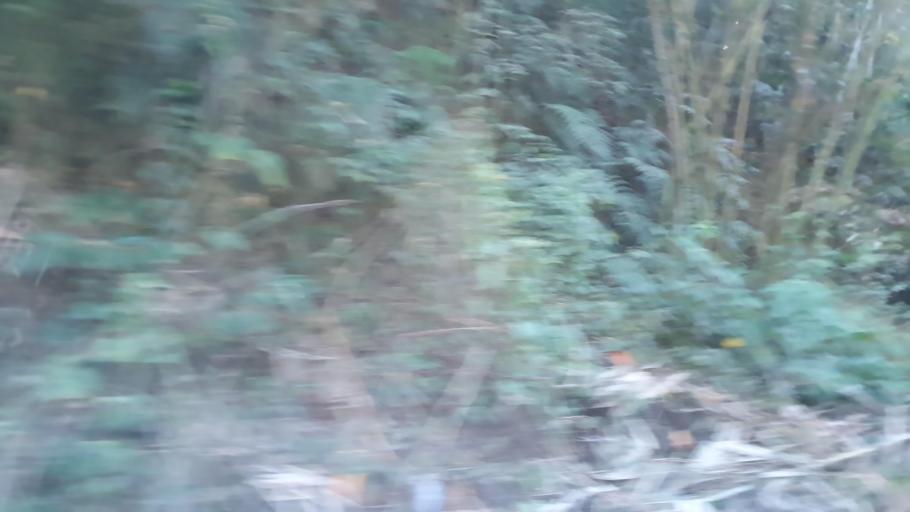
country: TW
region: Taiwan
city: Yujing
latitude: 23.0262
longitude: 120.3919
